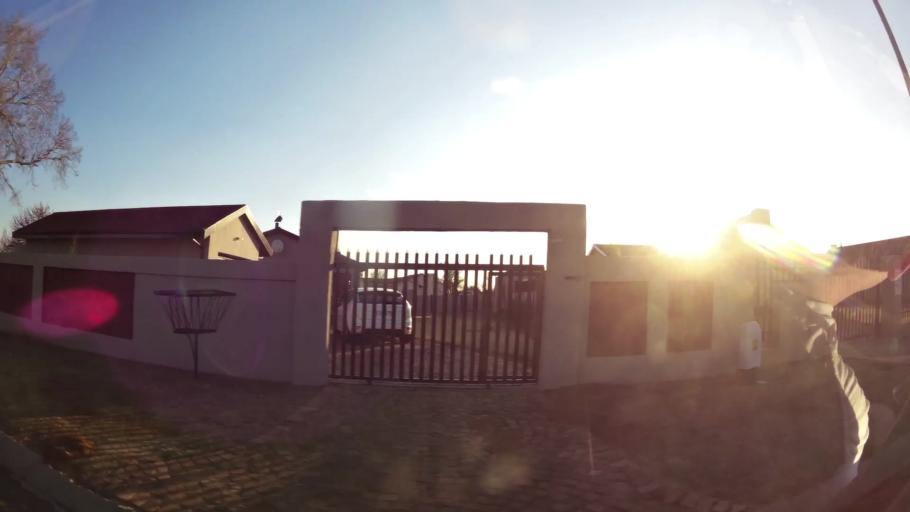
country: ZA
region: Gauteng
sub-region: West Rand District Municipality
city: Randfontein
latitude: -26.2069
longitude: 27.6520
